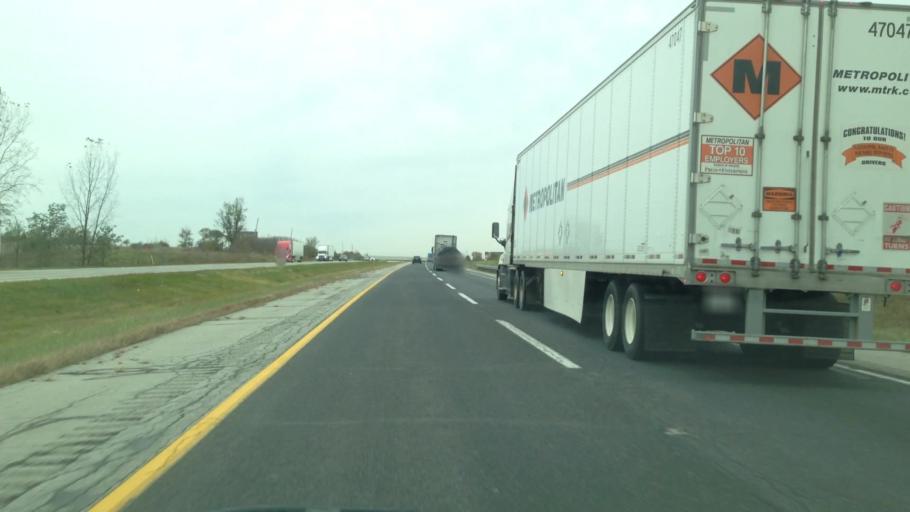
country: US
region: Indiana
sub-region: Steuben County
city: Fremont
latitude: 41.6758
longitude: -84.8710
